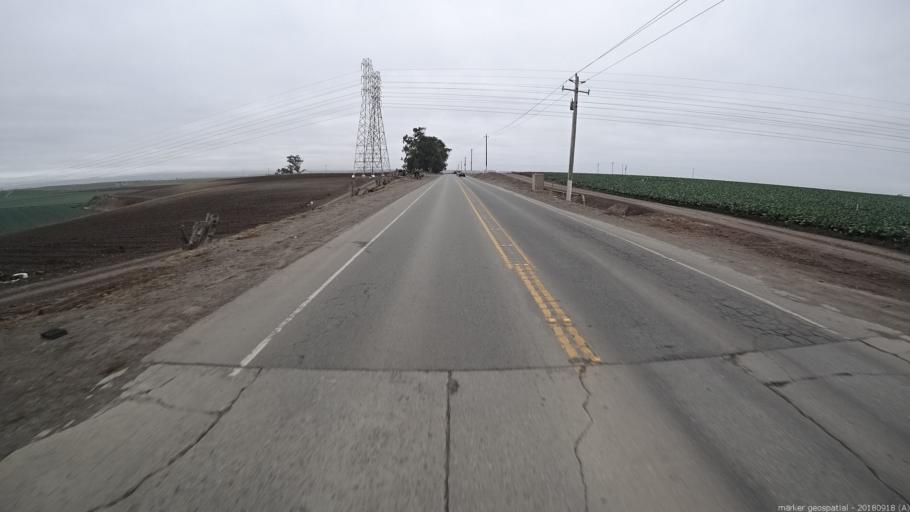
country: US
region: California
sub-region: Monterey County
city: Castroville
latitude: 36.7469
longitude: -121.7253
